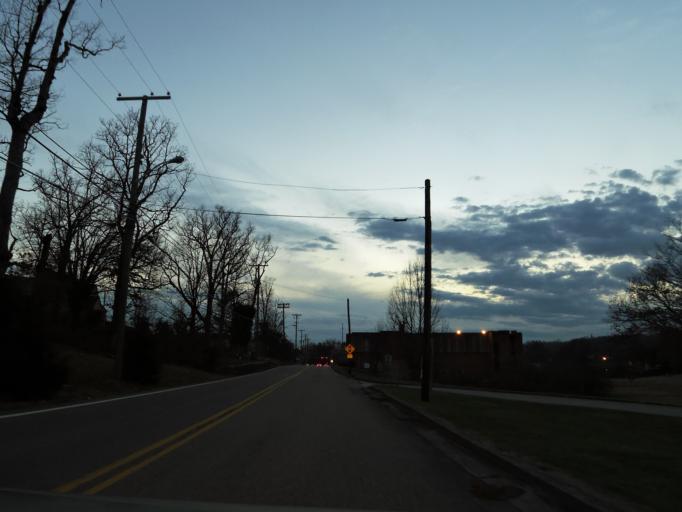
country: US
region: Tennessee
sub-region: Knox County
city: Knoxville
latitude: 35.9360
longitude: -83.9032
